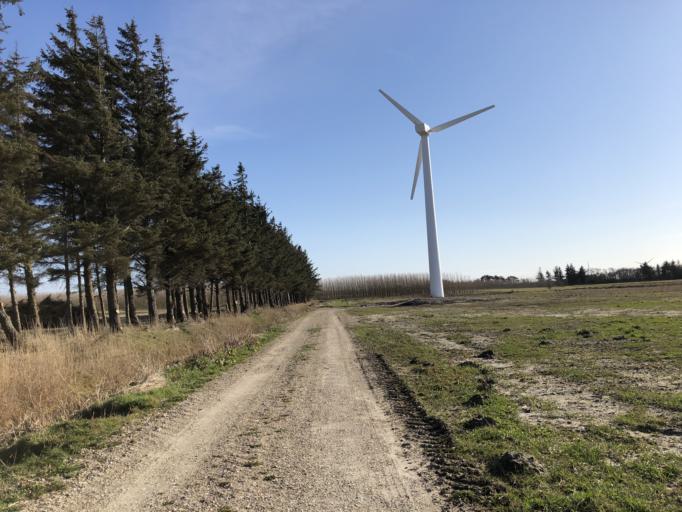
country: DK
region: Central Jutland
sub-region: Holstebro Kommune
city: Ulfborg
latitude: 56.3243
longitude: 8.3280
